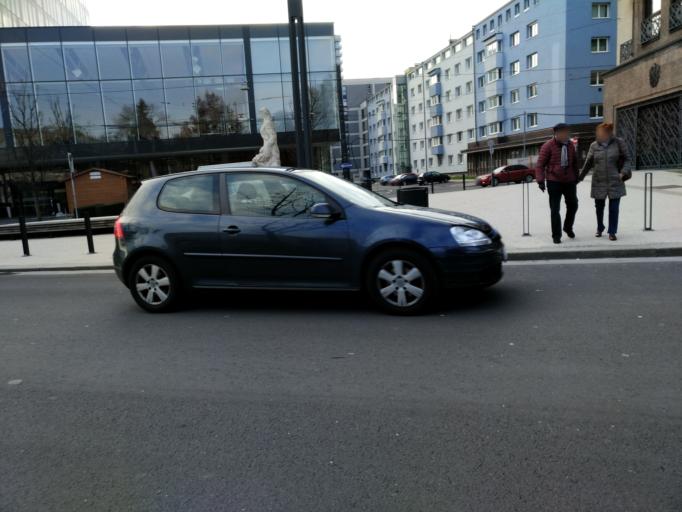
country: AT
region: Upper Austria
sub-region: Linz Stadt
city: Linz
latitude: 48.2939
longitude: 14.2916
